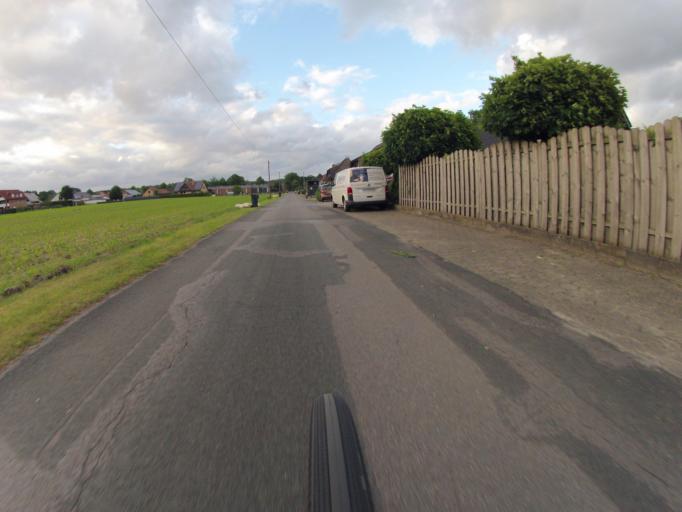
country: DE
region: North Rhine-Westphalia
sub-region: Regierungsbezirk Munster
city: Birgte
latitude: 52.2928
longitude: 7.6605
